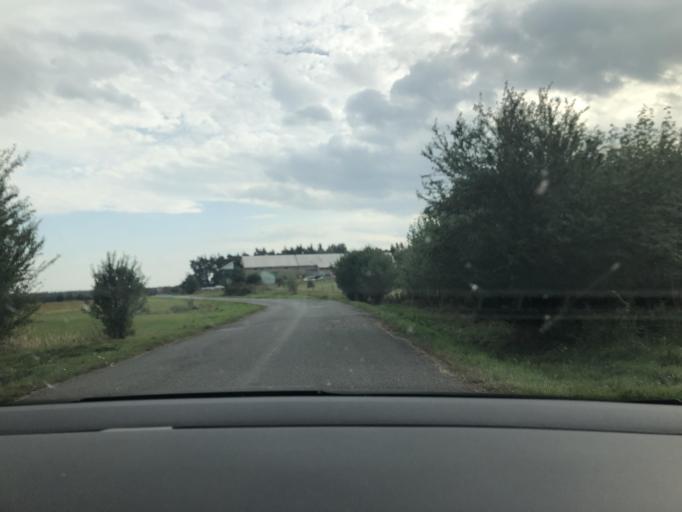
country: CZ
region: Pardubicky
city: Chvaletice
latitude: 50.0877
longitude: 15.4426
